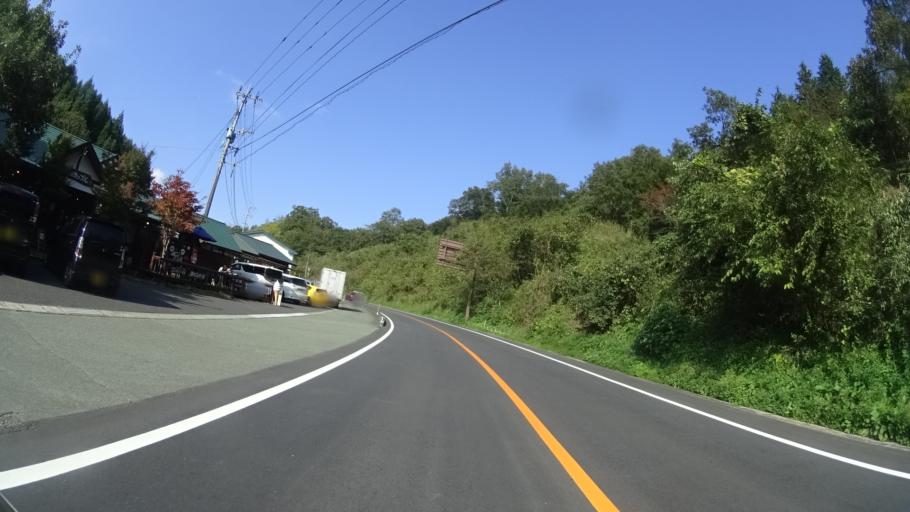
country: JP
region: Oita
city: Tsukawaki
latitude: 33.1654
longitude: 131.1133
